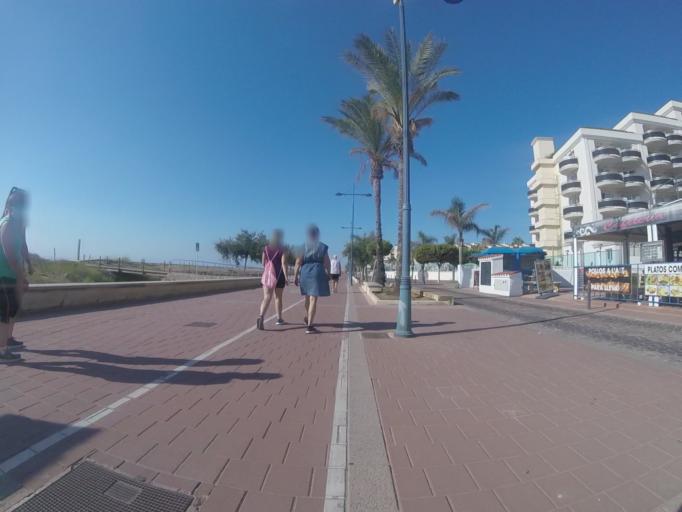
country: ES
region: Valencia
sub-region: Provincia de Castello
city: Benicarlo
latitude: 40.3970
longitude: 0.4155
